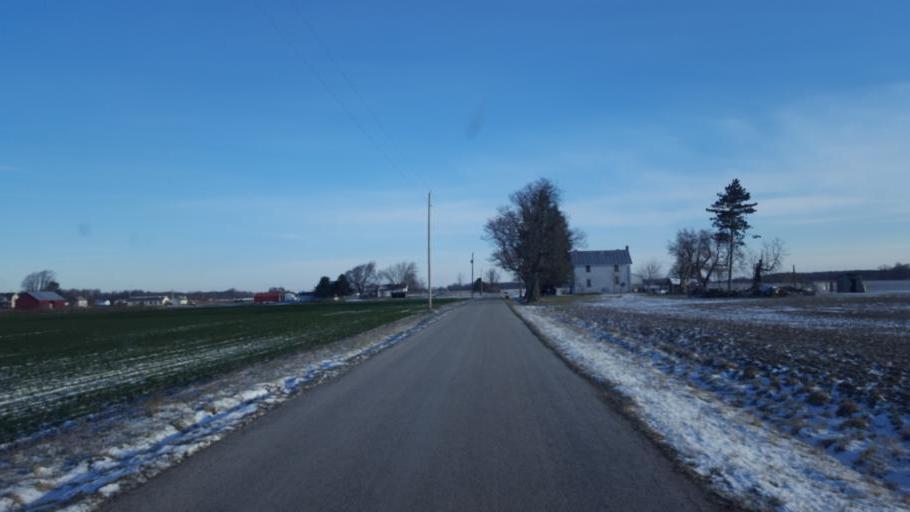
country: US
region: Ohio
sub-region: Morrow County
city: Cardington
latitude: 40.5546
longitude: -82.9337
